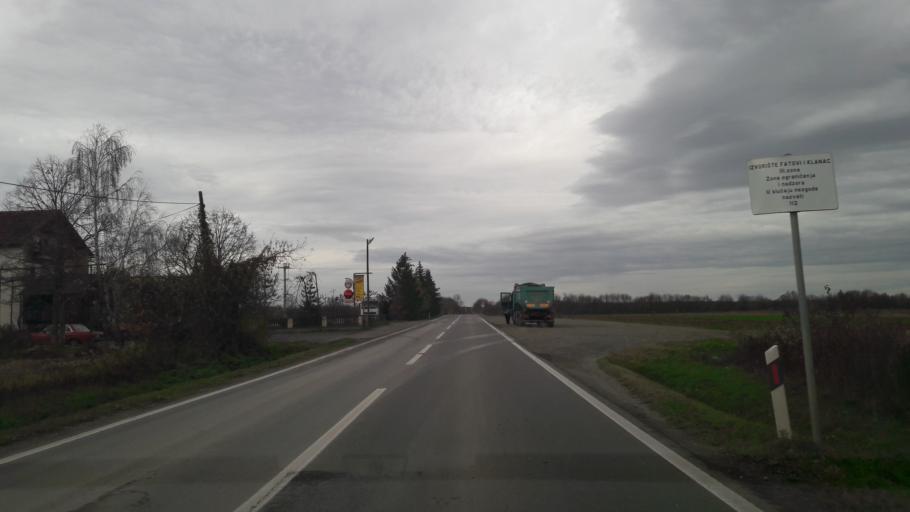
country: HR
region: Osjecko-Baranjska
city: Fericanci
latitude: 45.5331
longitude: 17.9436
